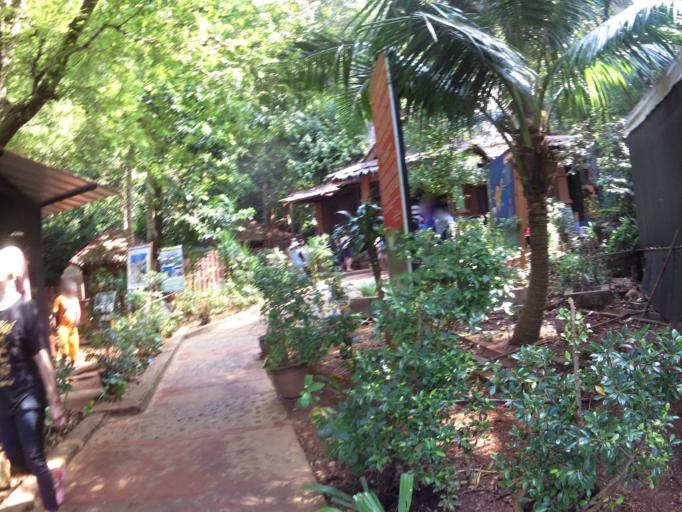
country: MY
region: Kedah
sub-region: Langkawi
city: Kuah
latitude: 6.2085
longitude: 99.7826
